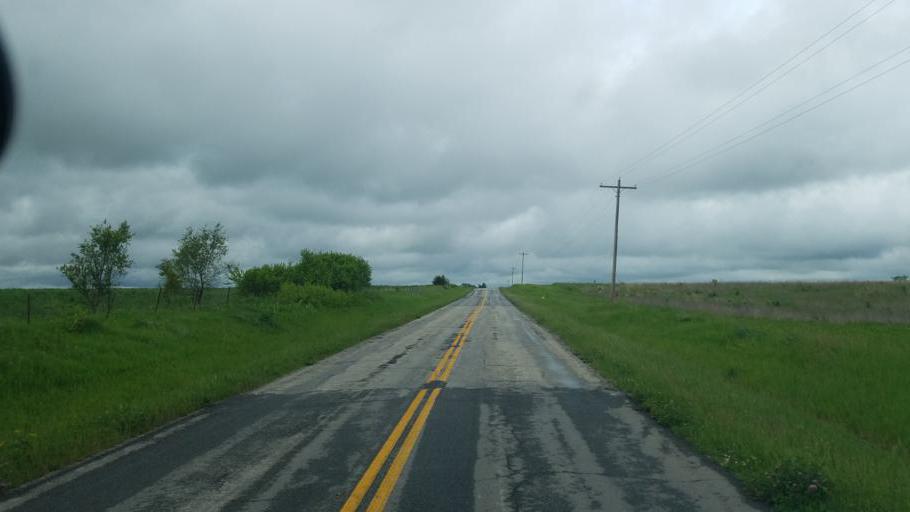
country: US
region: Missouri
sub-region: Mercer County
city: Princeton
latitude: 40.4212
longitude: -93.6847
